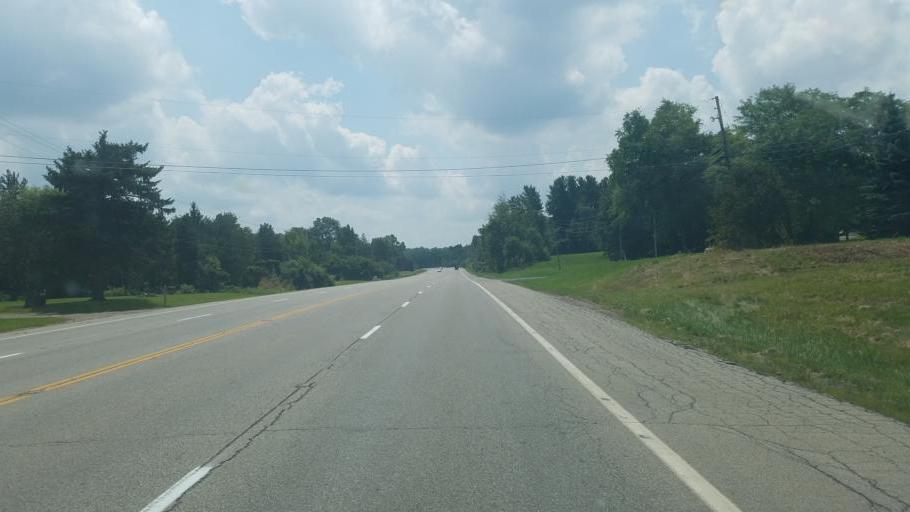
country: US
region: Ohio
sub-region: Richland County
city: Ontario
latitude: 40.7971
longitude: -82.5691
